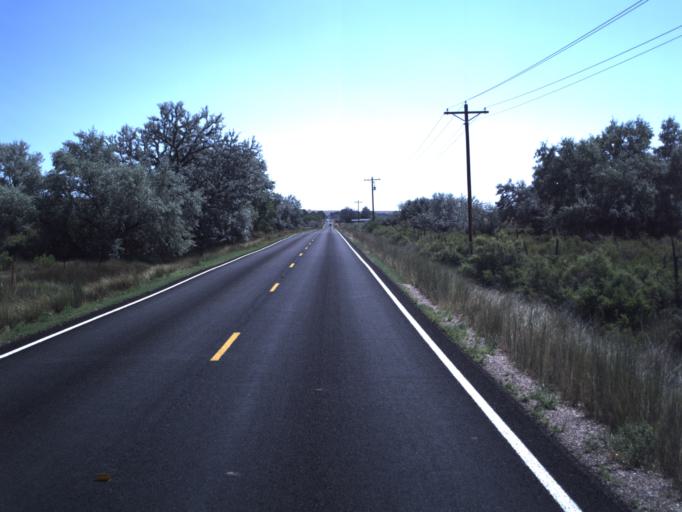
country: US
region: Utah
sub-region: Duchesne County
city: Roosevelt
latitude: 40.4037
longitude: -109.8343
